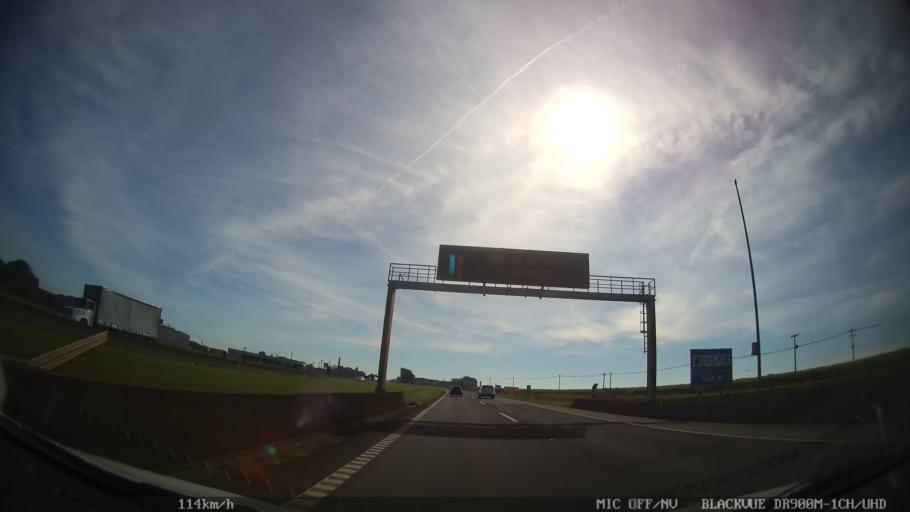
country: BR
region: Sao Paulo
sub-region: Araras
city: Araras
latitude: -22.4169
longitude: -47.3906
